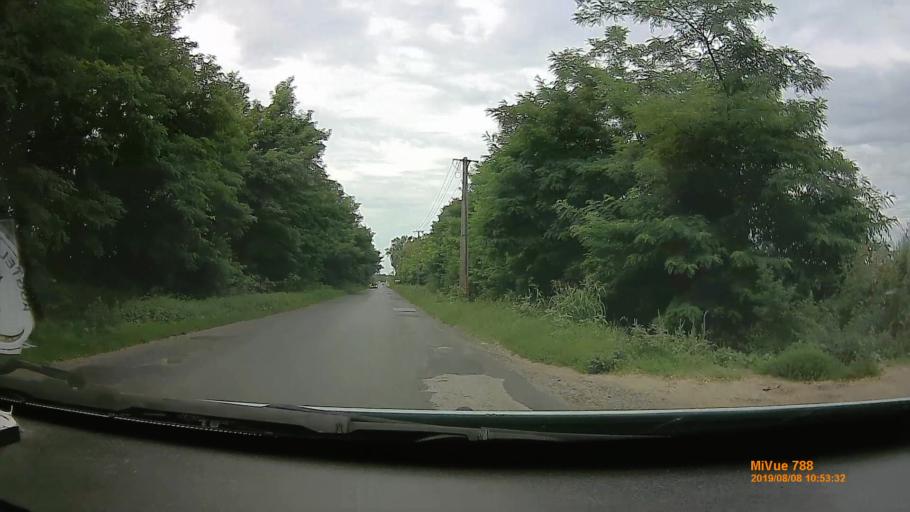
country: HU
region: Szabolcs-Szatmar-Bereg
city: Balkany
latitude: 47.7695
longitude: 21.8305
